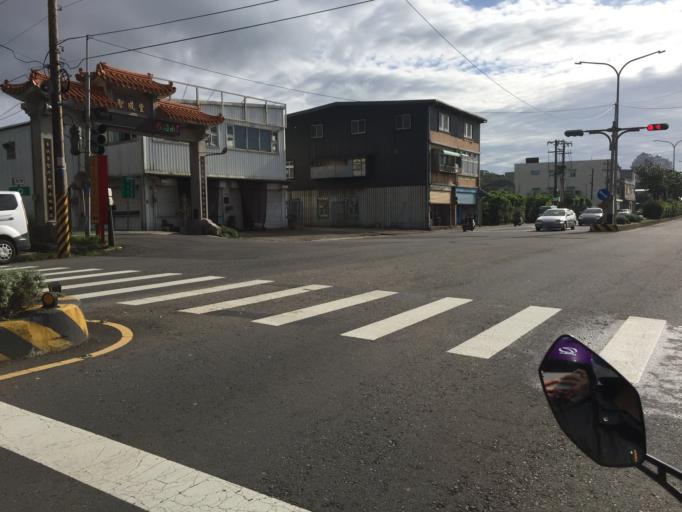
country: TW
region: Taipei
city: Taipei
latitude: 25.2589
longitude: 121.4773
